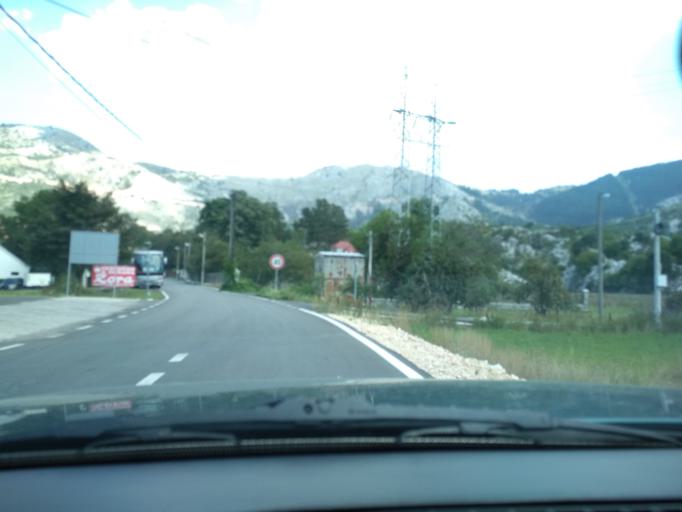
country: ME
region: Kotor
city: Kotor
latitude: 42.4306
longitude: 18.8273
